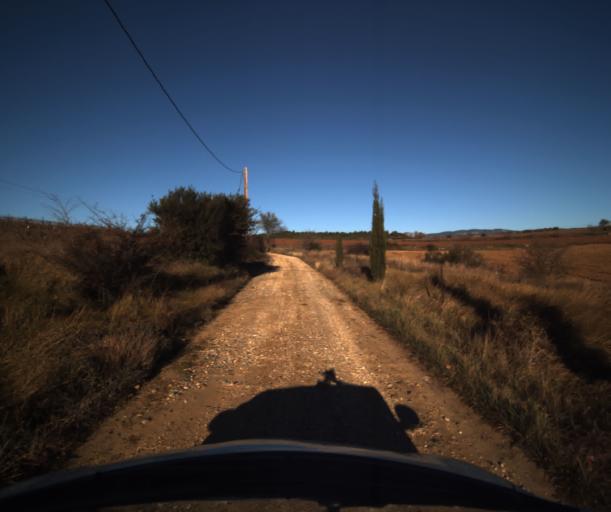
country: FR
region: Provence-Alpes-Cote d'Azur
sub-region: Departement du Vaucluse
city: Pertuis
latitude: 43.7193
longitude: 5.4891
